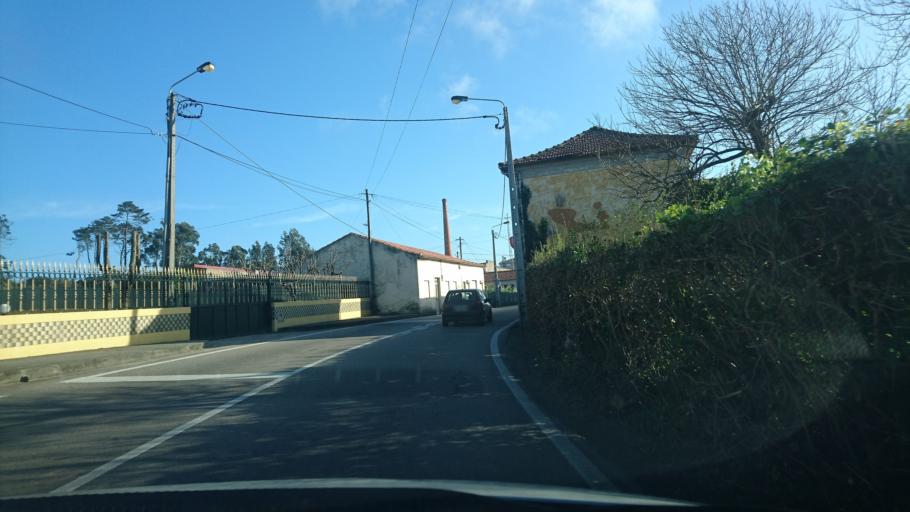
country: PT
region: Aveiro
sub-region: Ovar
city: Esmoriz
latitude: 40.9697
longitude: -8.6293
